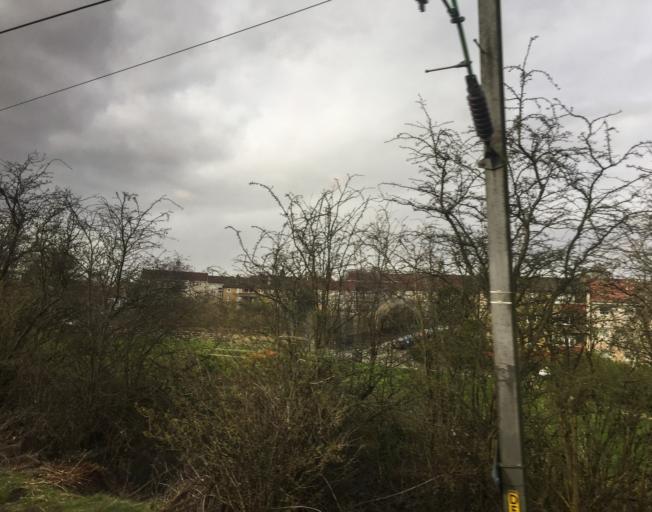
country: GB
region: Scotland
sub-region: East Dunbartonshire
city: Bearsden
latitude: 55.9060
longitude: -4.3520
